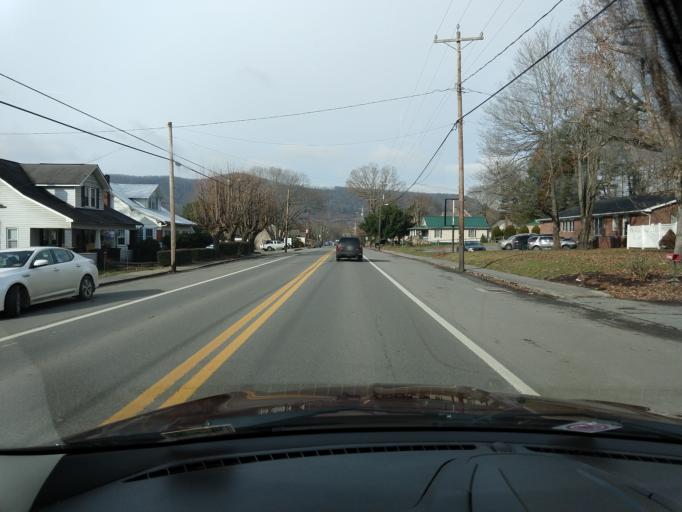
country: US
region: West Virginia
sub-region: Greenbrier County
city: Rainelle
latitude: 37.9637
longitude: -80.6928
